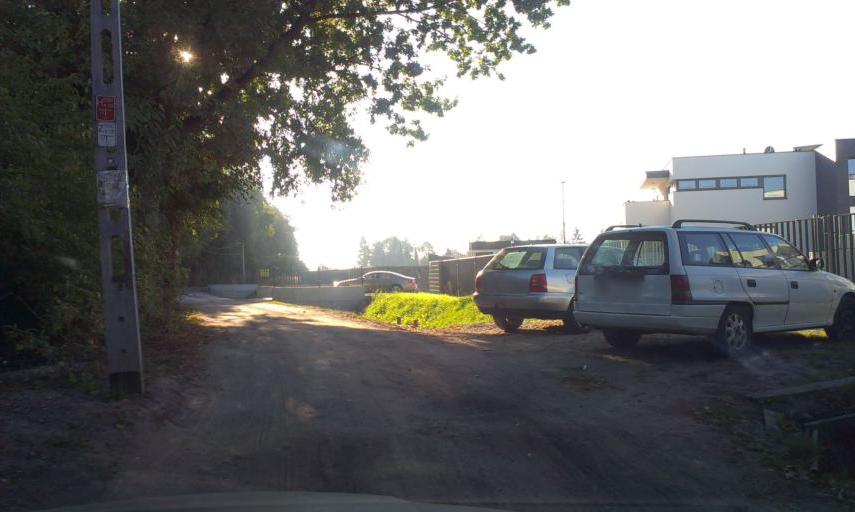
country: PL
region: Masovian Voivodeship
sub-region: Warszawa
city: Kabaty
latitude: 52.1167
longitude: 21.0998
